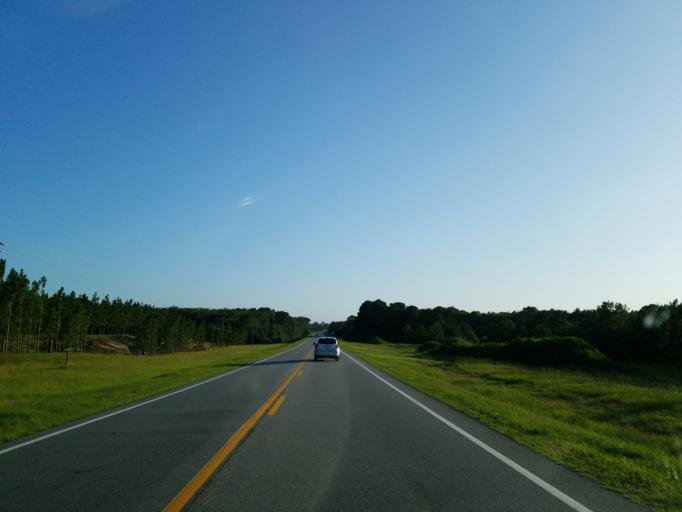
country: US
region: Georgia
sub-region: Irwin County
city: Ocilla
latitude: 31.6356
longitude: -83.4128
